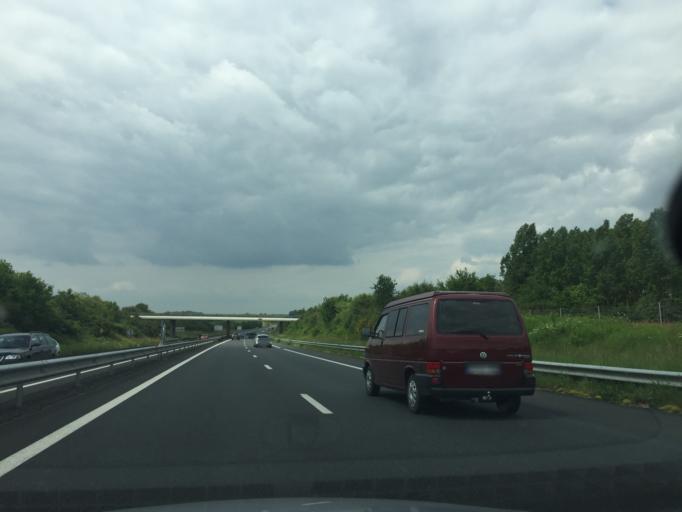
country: FR
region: Pays de la Loire
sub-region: Departement de la Vendee
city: Les Essarts
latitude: 46.7840
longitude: -1.1947
